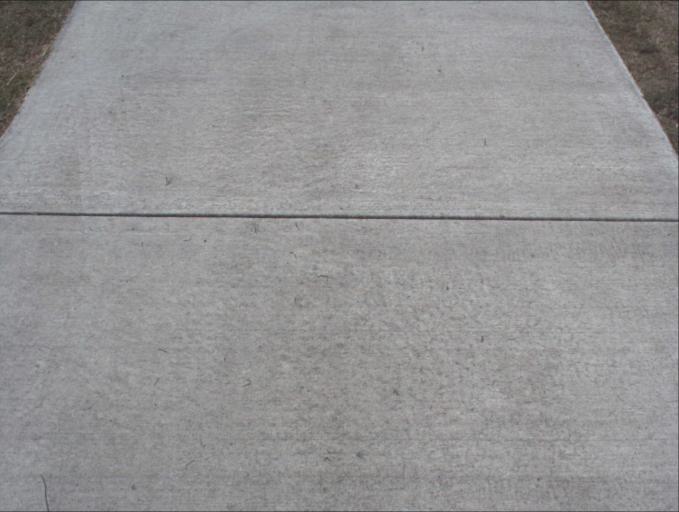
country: AU
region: Queensland
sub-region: Logan
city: Beenleigh
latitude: -27.6777
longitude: 153.1858
